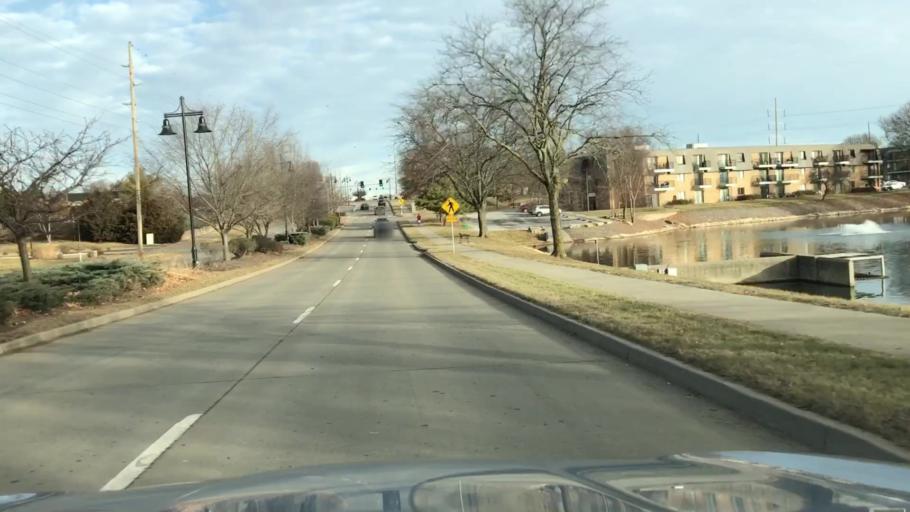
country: US
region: Missouri
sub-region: Jackson County
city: Lees Summit
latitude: 38.9222
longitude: -94.4128
